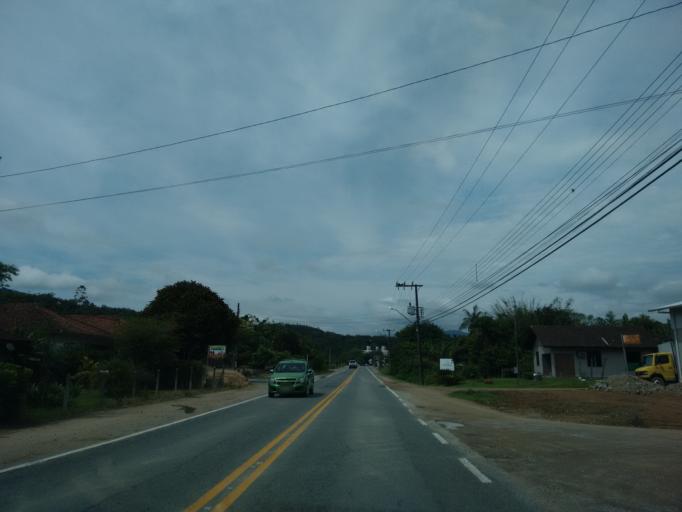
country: BR
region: Santa Catarina
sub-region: Pomerode
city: Pomerode
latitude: -26.6835
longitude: -49.1484
